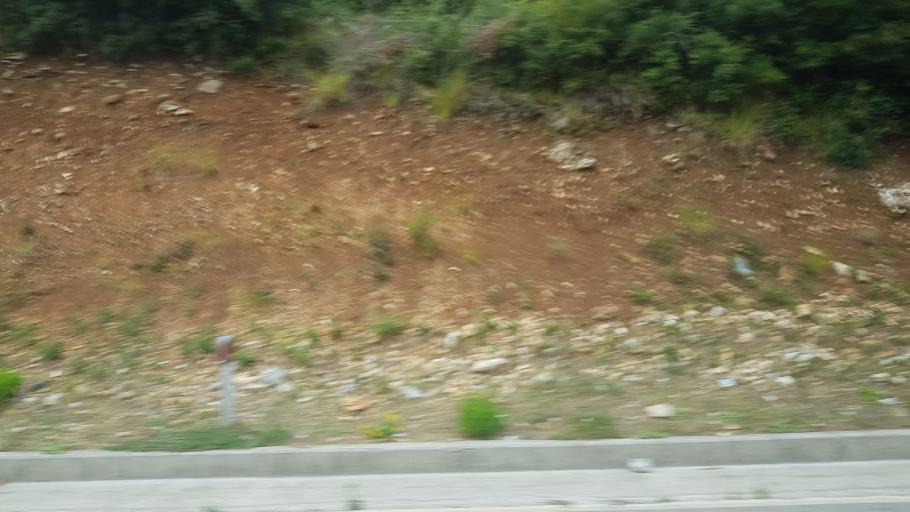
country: AL
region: Fier
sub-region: Rrethi i Mallakastres
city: Kute
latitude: 40.5118
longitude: 19.7515
